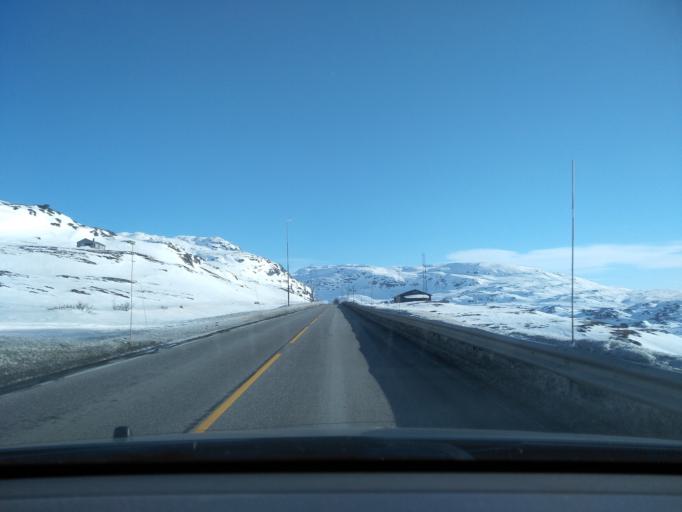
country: NO
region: Aust-Agder
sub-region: Bykle
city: Hovden
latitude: 59.8416
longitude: 6.9802
